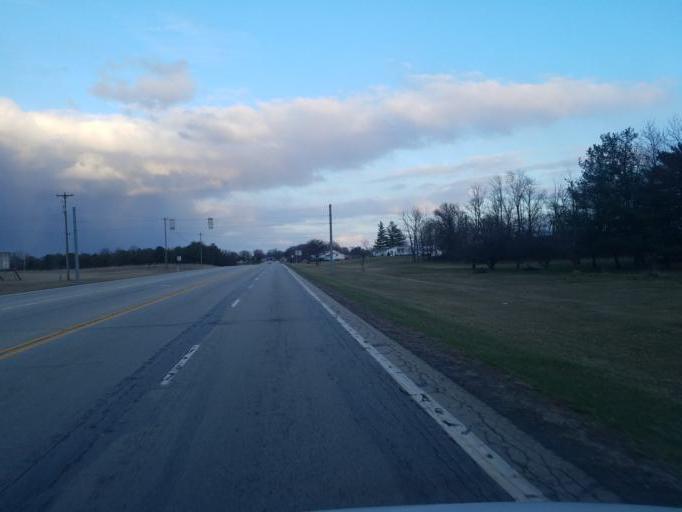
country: US
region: Indiana
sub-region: Henry County
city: Knightstown
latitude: 39.8021
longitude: -85.4475
